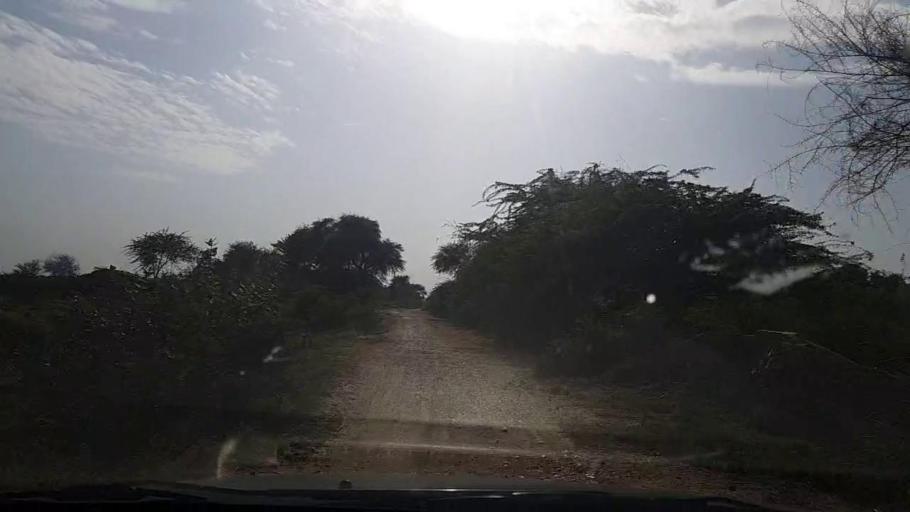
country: PK
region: Sindh
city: Mirpur Batoro
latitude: 24.5541
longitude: 68.1799
